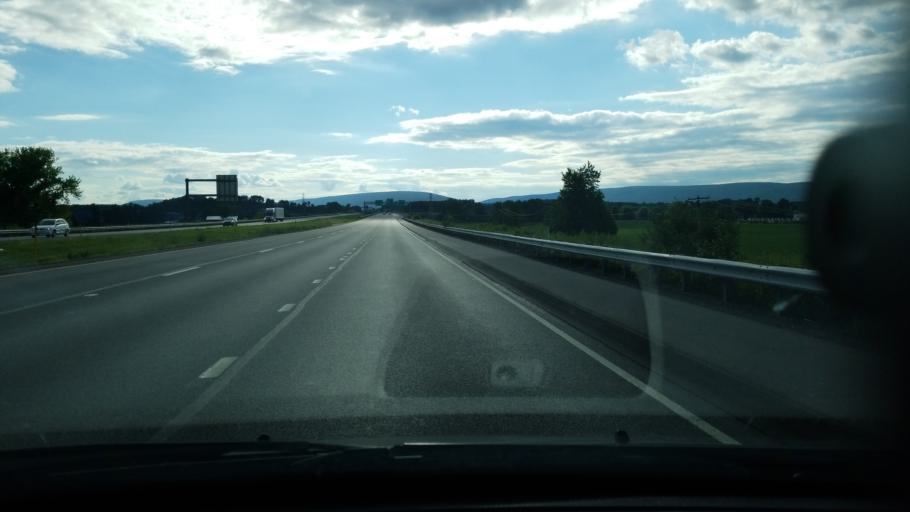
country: US
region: Pennsylvania
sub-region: Union County
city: New Columbia
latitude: 41.0521
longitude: -76.8588
